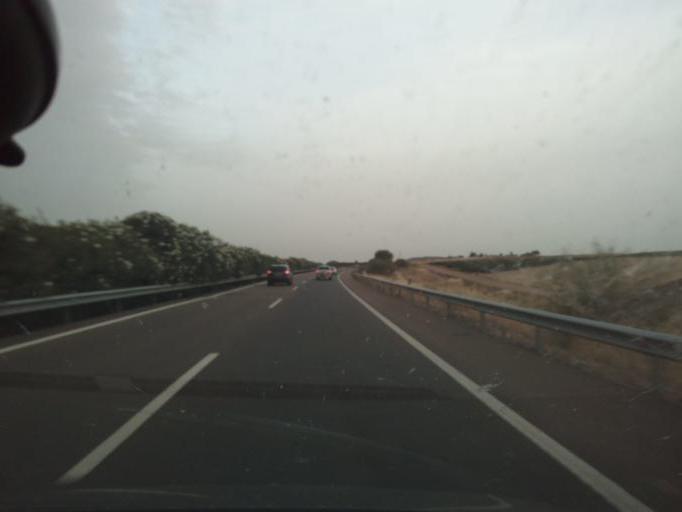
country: ES
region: Extremadura
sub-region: Provincia de Badajoz
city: Trujillanos
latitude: 38.9449
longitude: -6.3023
